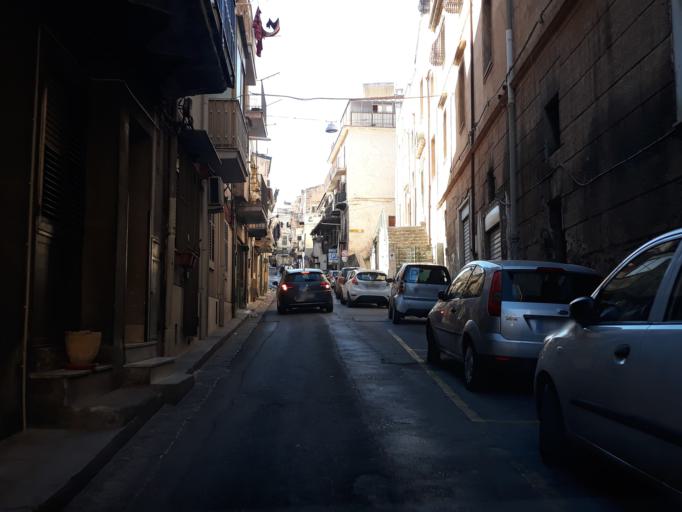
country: IT
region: Sicily
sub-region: Palermo
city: Monreale
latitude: 38.0848
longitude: 13.2941
